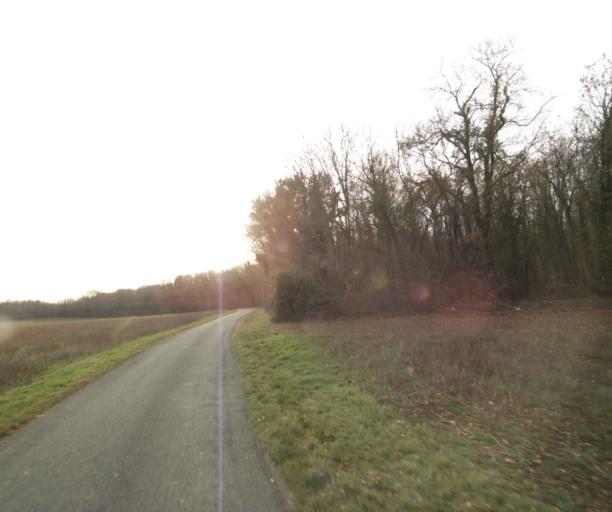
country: FR
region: Poitou-Charentes
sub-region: Departement de la Charente-Maritime
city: Saint-Hilaire-de-Villefranche
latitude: 45.8314
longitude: -0.5697
